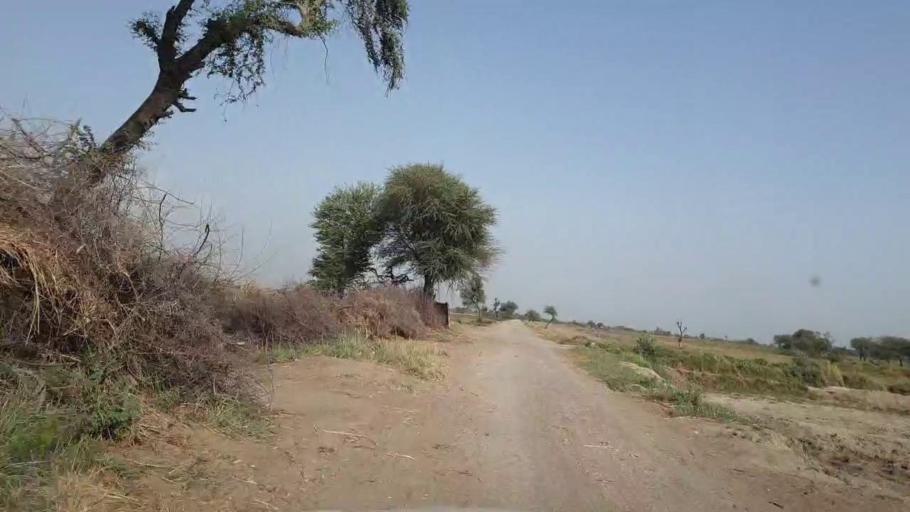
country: PK
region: Sindh
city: Tando Ghulam Ali
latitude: 25.0762
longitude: 68.8480
